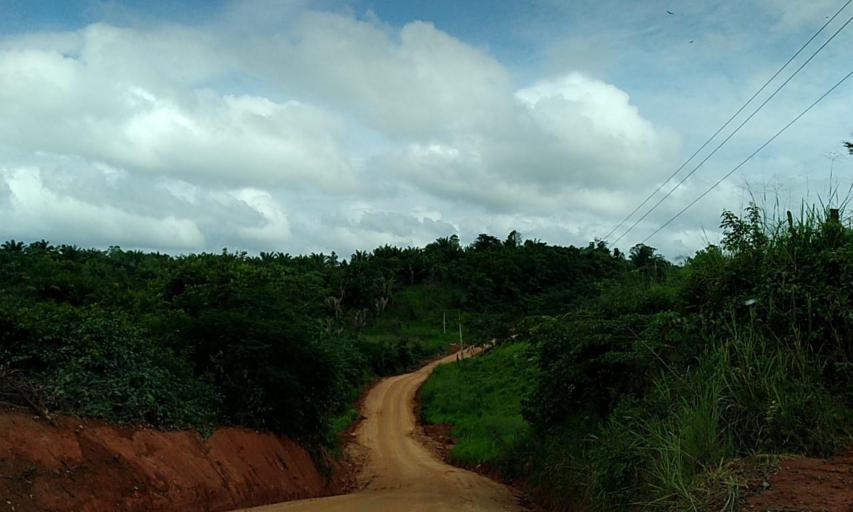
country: BR
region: Para
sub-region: Senador Jose Porfirio
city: Senador Jose Porfirio
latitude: -3.0785
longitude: -51.6346
